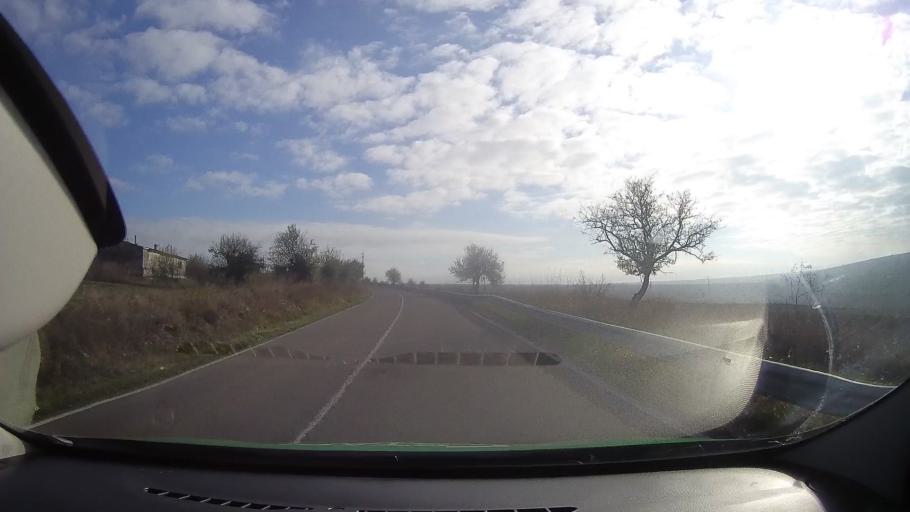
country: RO
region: Tulcea
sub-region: Comuna Bestepe
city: Bestepe
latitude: 45.0818
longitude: 29.0257
